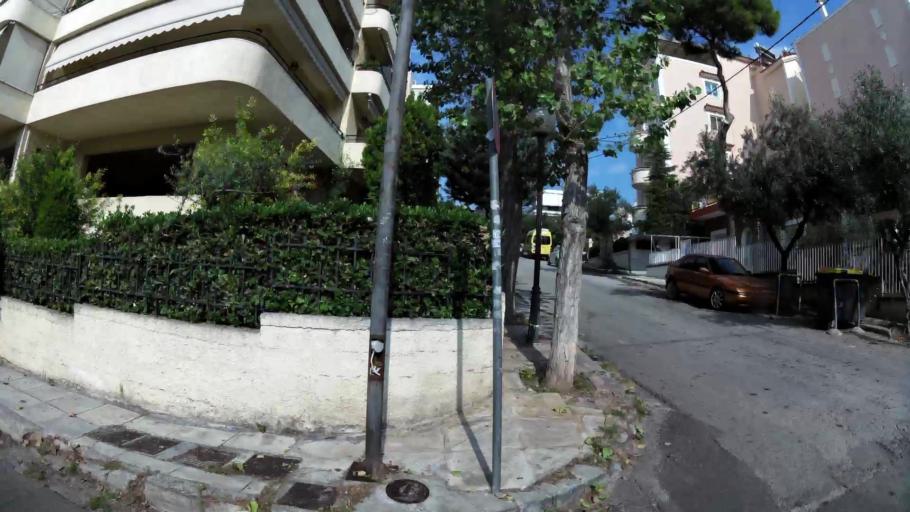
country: GR
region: Attica
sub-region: Nomarchia Athinas
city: Irakleio
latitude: 38.0503
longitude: 23.7560
